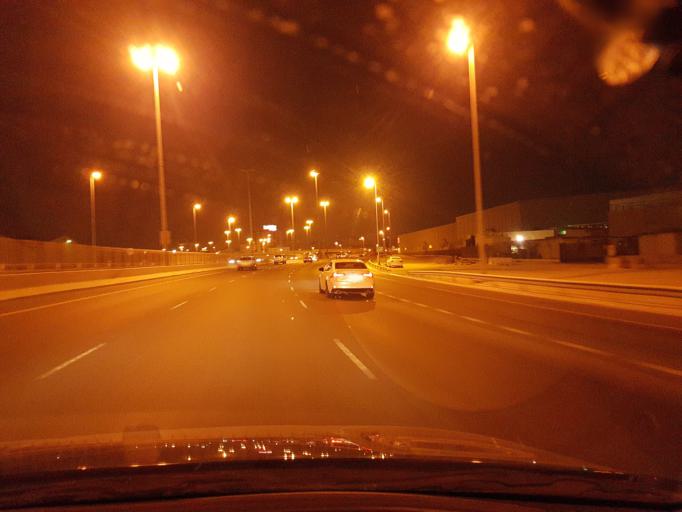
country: BH
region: Manama
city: Manama
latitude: 26.2035
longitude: 50.6083
